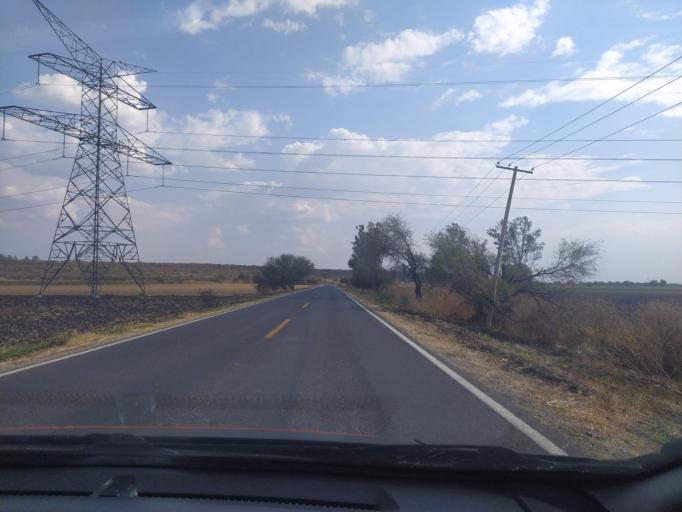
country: MX
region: Guanajuato
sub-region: San Francisco del Rincon
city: San Ignacio de Hidalgo
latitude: 20.9328
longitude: -101.8529
